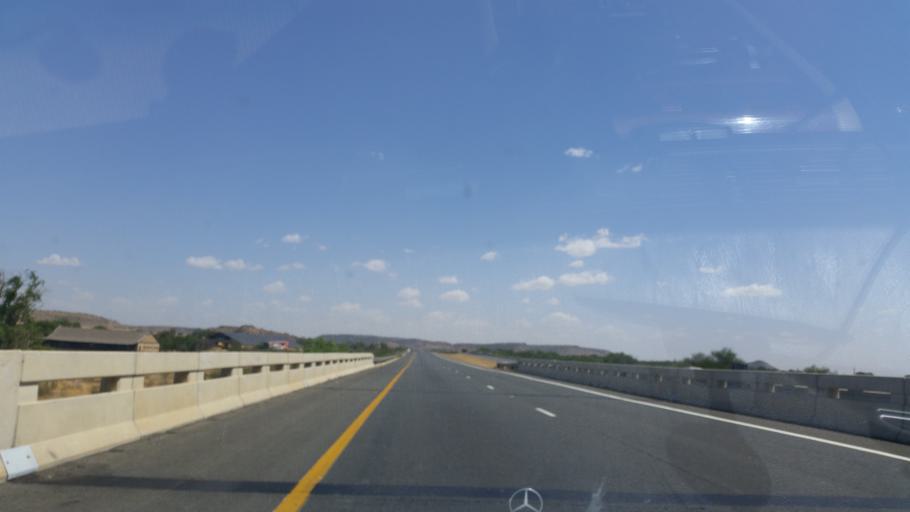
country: ZA
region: Orange Free State
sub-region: Mangaung Metropolitan Municipality
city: Bloemfontein
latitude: -28.9680
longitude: 26.3355
